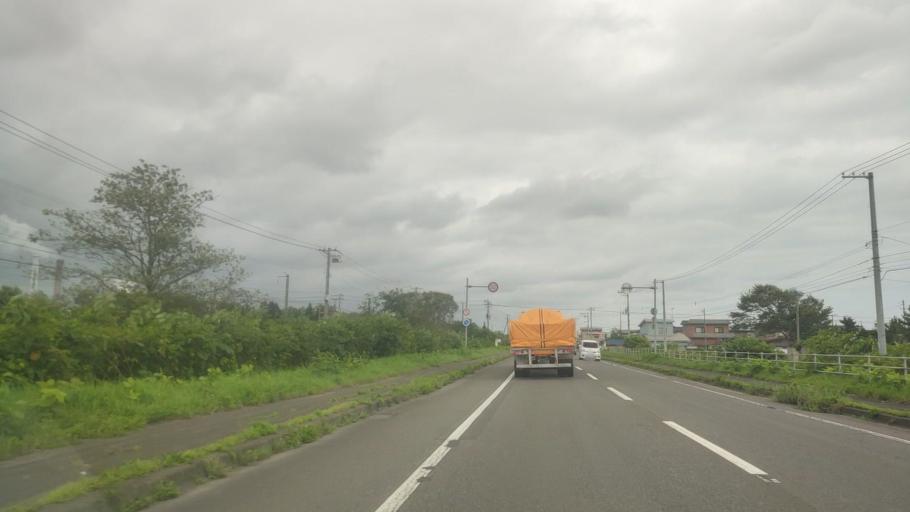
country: JP
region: Hokkaido
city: Shiraoi
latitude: 42.5053
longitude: 141.2808
